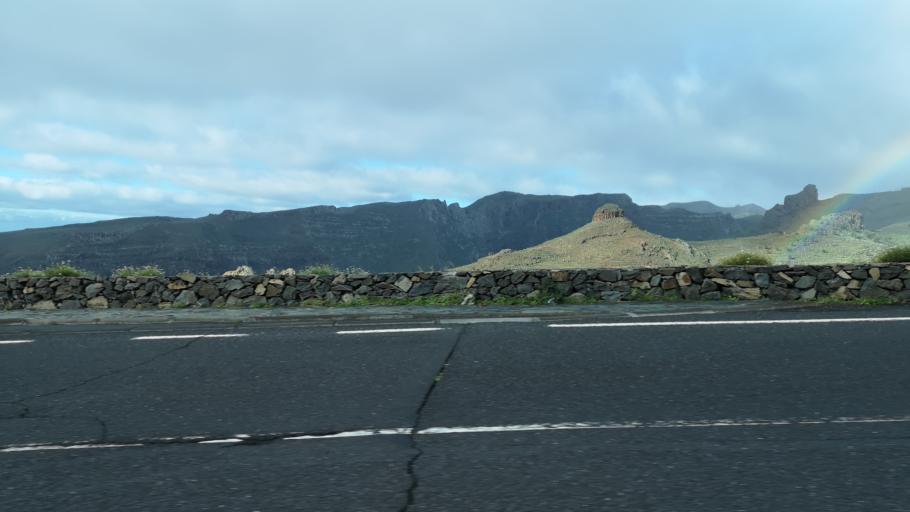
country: ES
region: Canary Islands
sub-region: Provincia de Santa Cruz de Tenerife
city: San Sebastian de la Gomera
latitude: 28.0904
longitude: -17.1516
